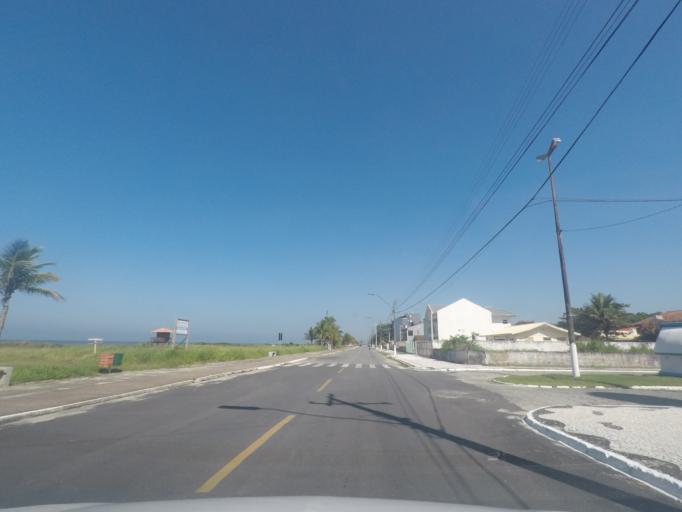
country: BR
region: Parana
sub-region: Pontal Do Parana
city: Pontal do Parana
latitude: -25.7216
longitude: -48.4832
